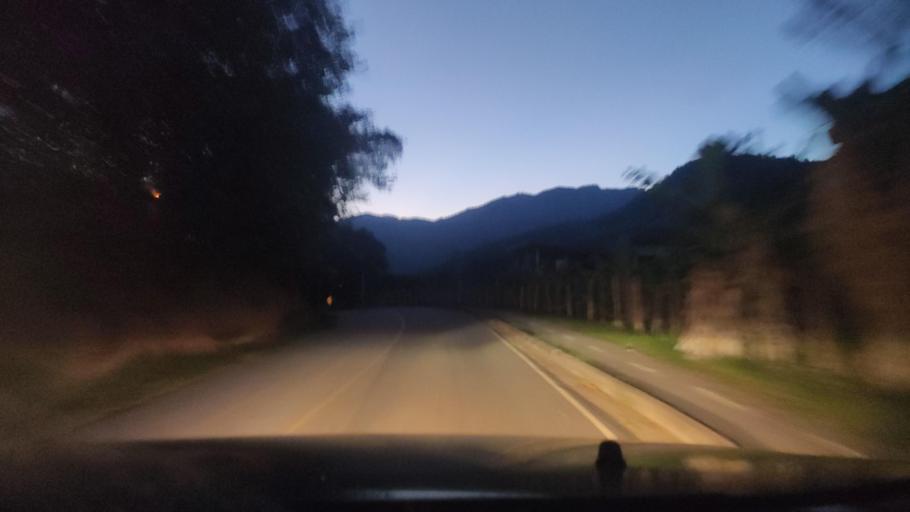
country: BR
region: Minas Gerais
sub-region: Paraisopolis
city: Paraisopolis
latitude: -22.7041
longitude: -45.7608
